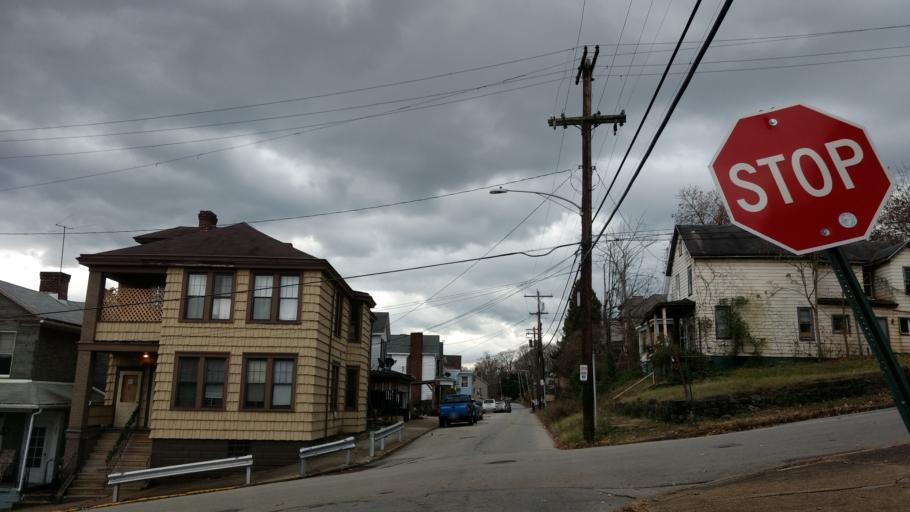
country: US
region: Pennsylvania
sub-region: Washington County
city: Charleroi
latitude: 40.1384
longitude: -79.9007
